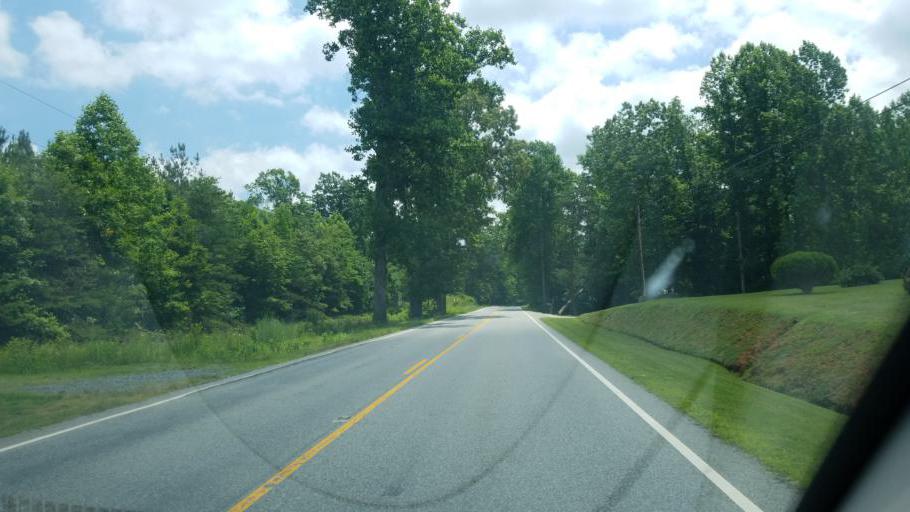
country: US
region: Virginia
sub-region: Nelson County
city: Lovingston
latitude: 37.5675
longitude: -78.8499
